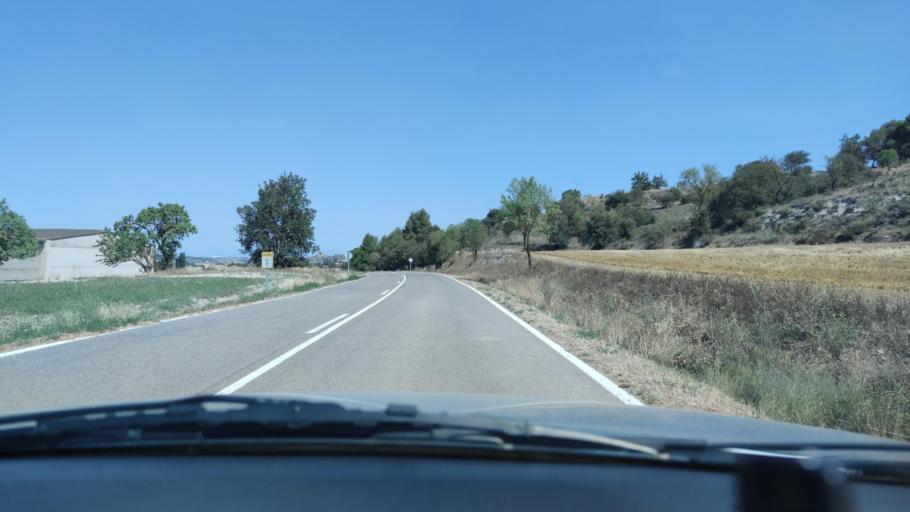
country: ES
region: Catalonia
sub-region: Provincia de Lleida
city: Sant Guim de Freixenet
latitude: 41.6229
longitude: 1.3494
